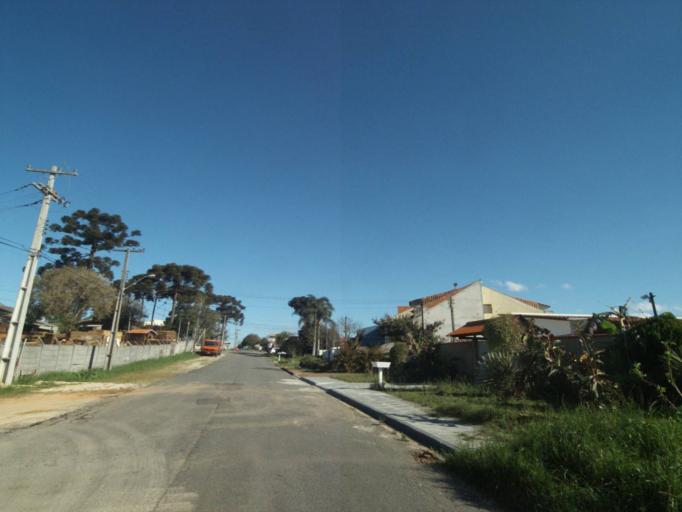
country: BR
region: Parana
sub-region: Curitiba
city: Curitiba
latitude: -25.3887
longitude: -49.2572
